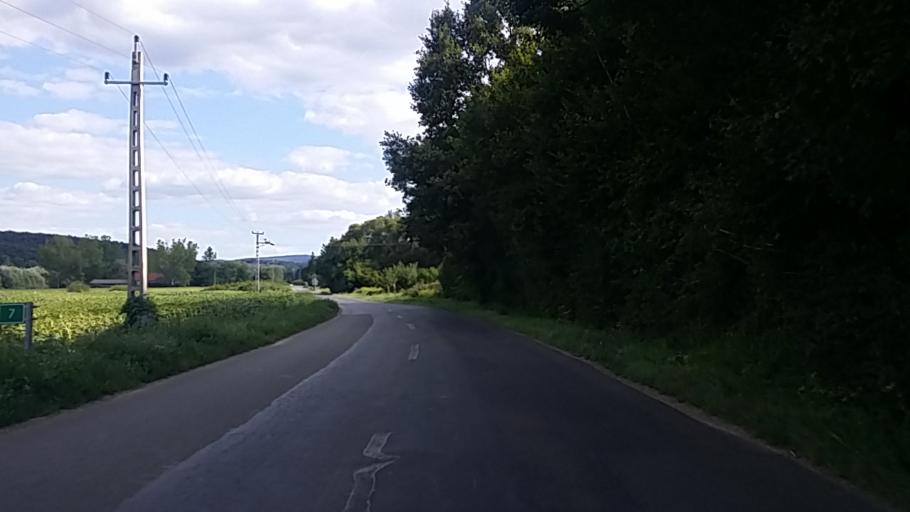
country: HU
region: Baranya
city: Sasd
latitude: 46.1805
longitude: 18.0842
